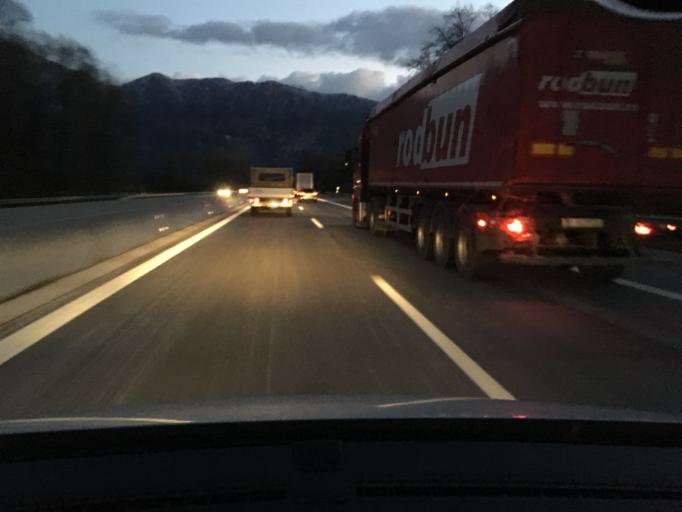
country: AT
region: Tyrol
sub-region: Politischer Bezirk Kufstein
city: Ebbs
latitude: 47.6369
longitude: 12.1952
